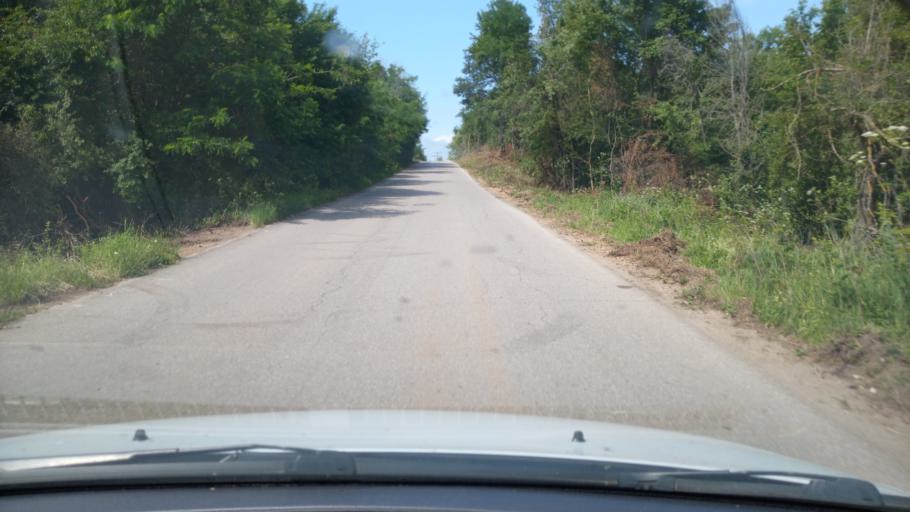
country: BG
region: Lovech
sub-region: Obshtina Lukovit
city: Lukovit
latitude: 43.1973
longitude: 24.1162
